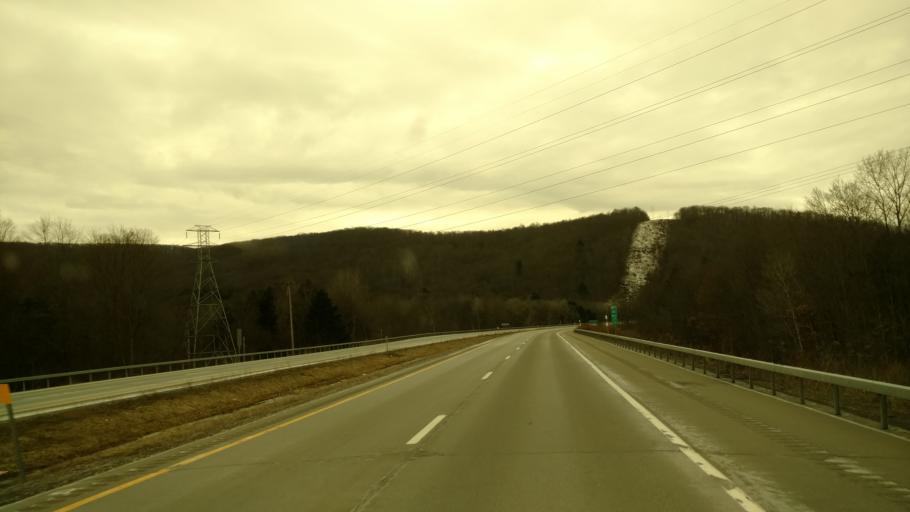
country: US
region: New York
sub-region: Cattaraugus County
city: Salamanca
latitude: 42.1016
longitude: -78.8042
